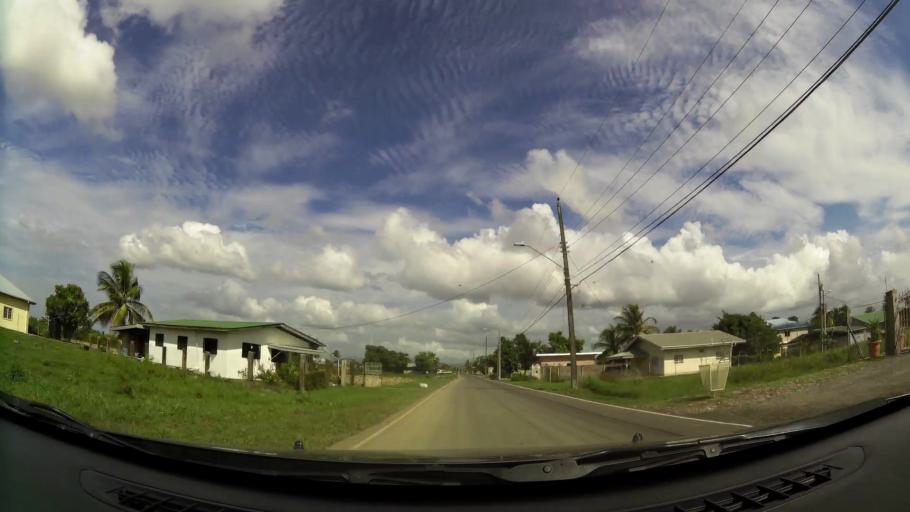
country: TT
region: Chaguanas
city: Chaguanas
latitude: 10.5393
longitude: -61.3886
